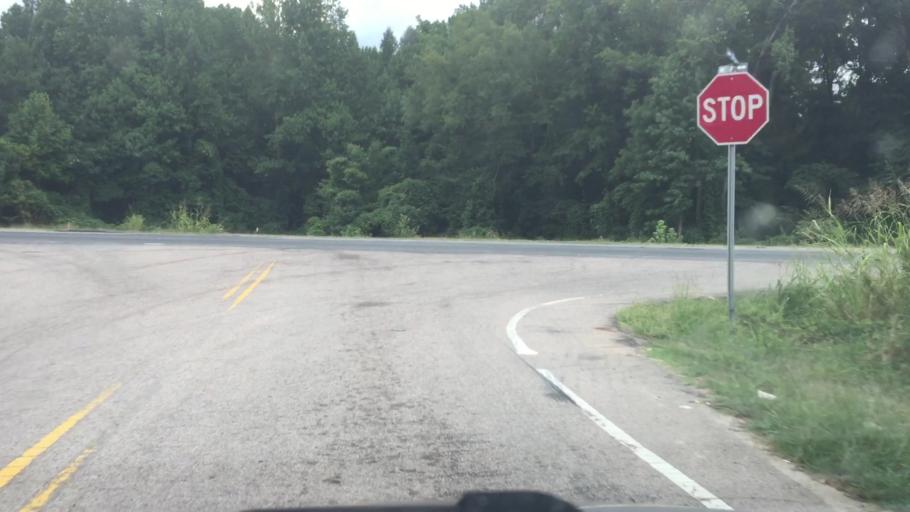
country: US
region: North Carolina
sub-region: Cabarrus County
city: Kannapolis
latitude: 35.4886
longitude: -80.6619
